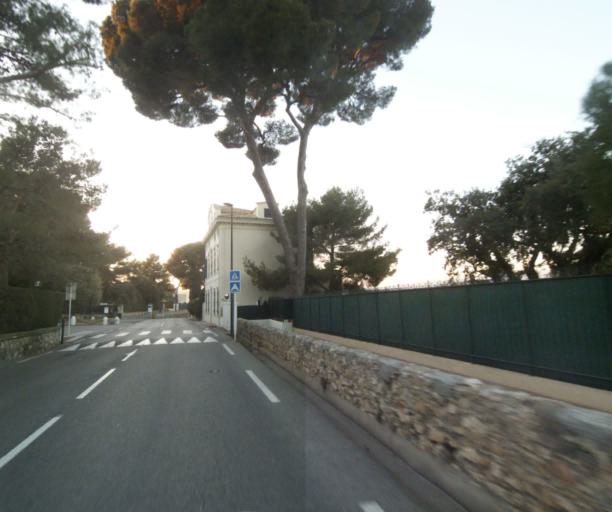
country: FR
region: Provence-Alpes-Cote d'Azur
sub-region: Departement des Alpes-Maritimes
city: Antibes
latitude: 43.5490
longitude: 7.1212
